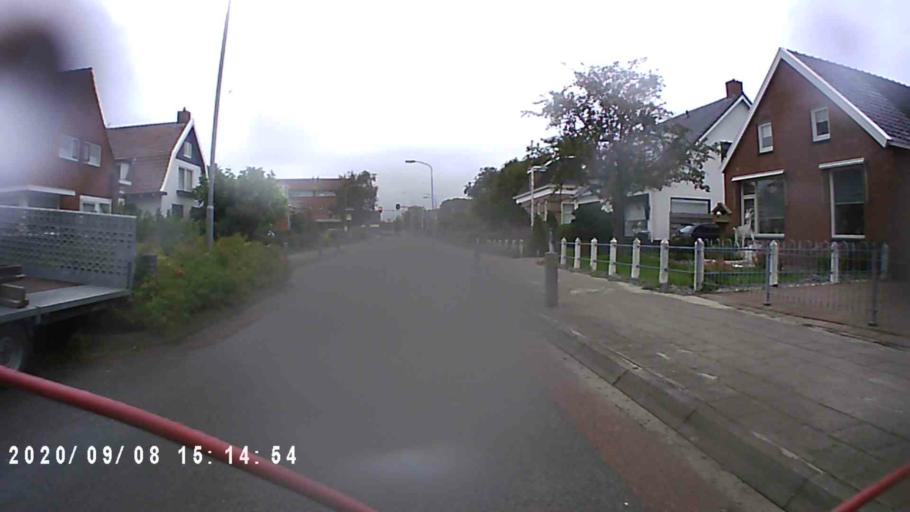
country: NL
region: Groningen
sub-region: Gemeente Bedum
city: Bedum
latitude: 53.2729
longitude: 6.7006
